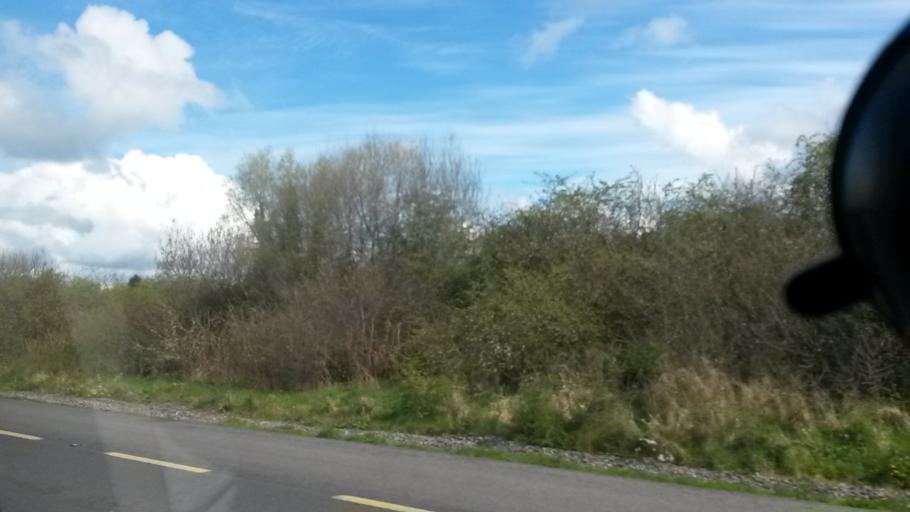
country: IE
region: Ulster
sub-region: An Cabhan
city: Belturbet
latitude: 54.1174
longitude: -7.4787
